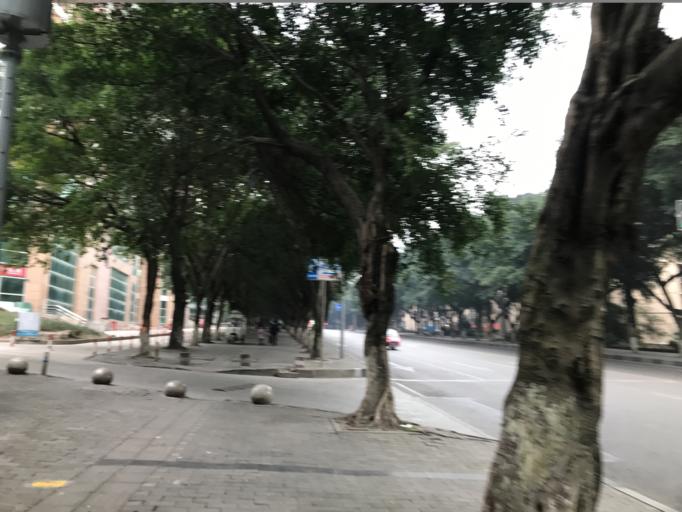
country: CN
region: Chongqing Shi
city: Chongqing
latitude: 29.5289
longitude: 106.5516
